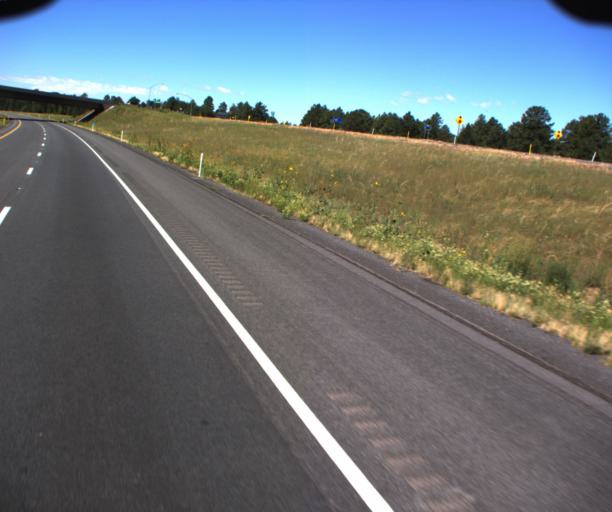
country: US
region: Arizona
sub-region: Coconino County
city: Williams
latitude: 35.2465
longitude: -112.2135
